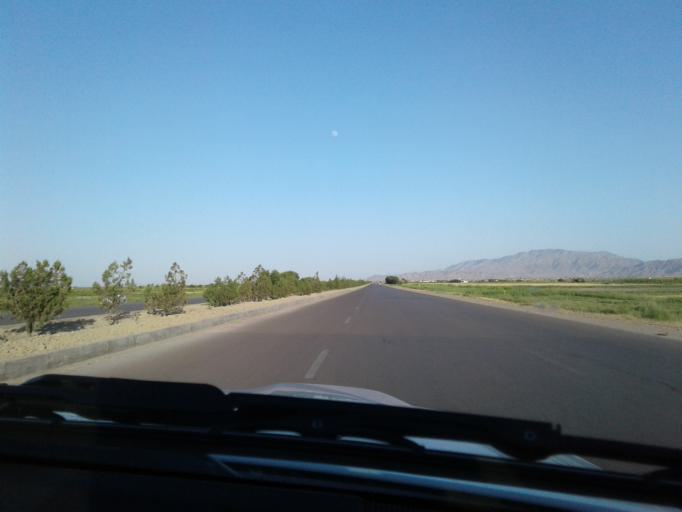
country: TM
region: Ahal
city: Baharly
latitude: 38.3451
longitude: 57.5569
